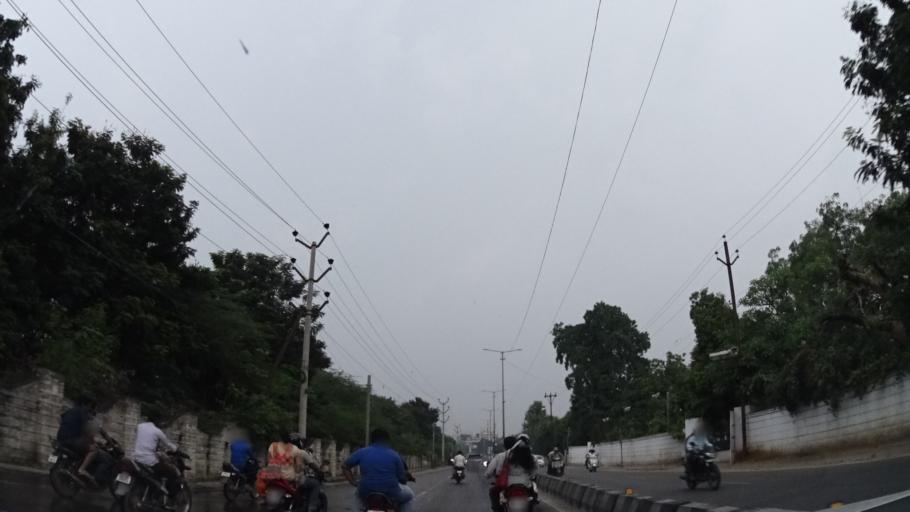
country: IN
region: Telangana
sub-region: Hyderabad
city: Malkajgiri
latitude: 17.4487
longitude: 78.4875
